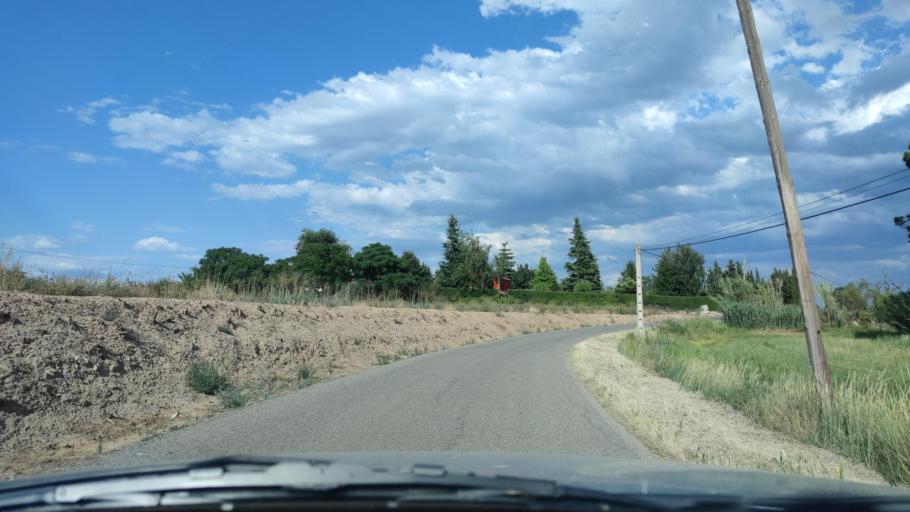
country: ES
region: Catalonia
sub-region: Provincia de Lleida
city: Lleida
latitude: 41.6300
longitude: 0.5856
